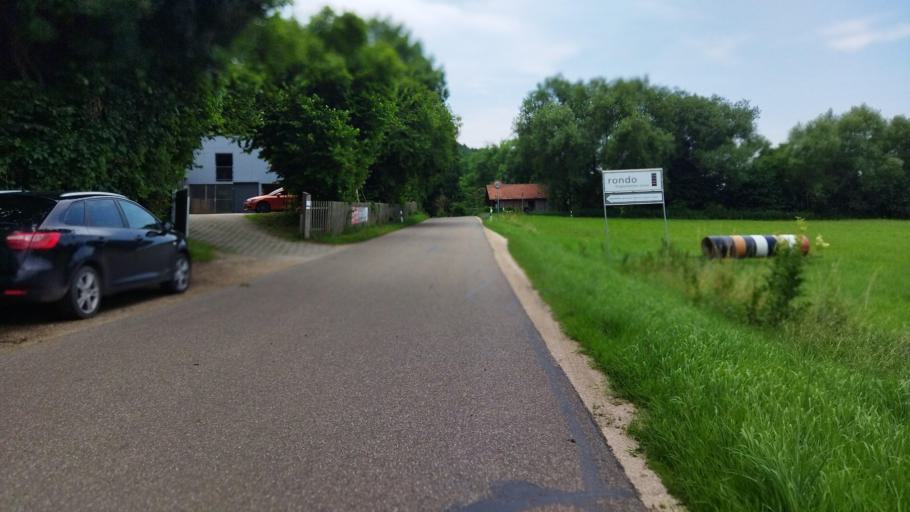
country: DE
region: Bavaria
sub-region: Upper Palatinate
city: Pentling
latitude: 48.9845
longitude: 12.0462
